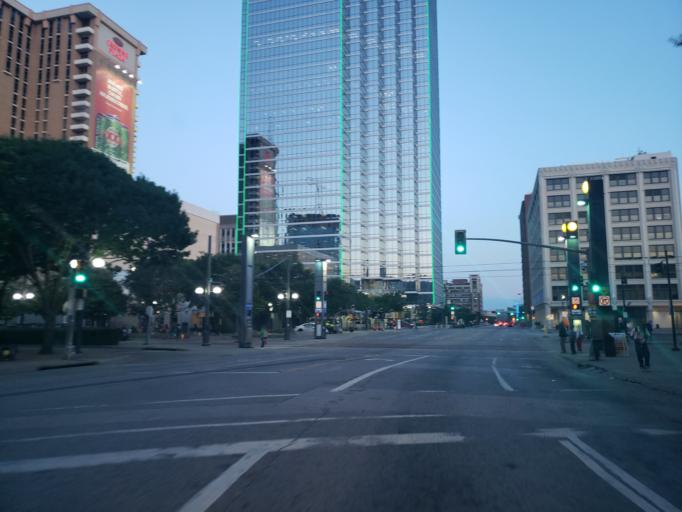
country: US
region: Texas
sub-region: Dallas County
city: Dallas
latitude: 32.7814
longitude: -96.8049
